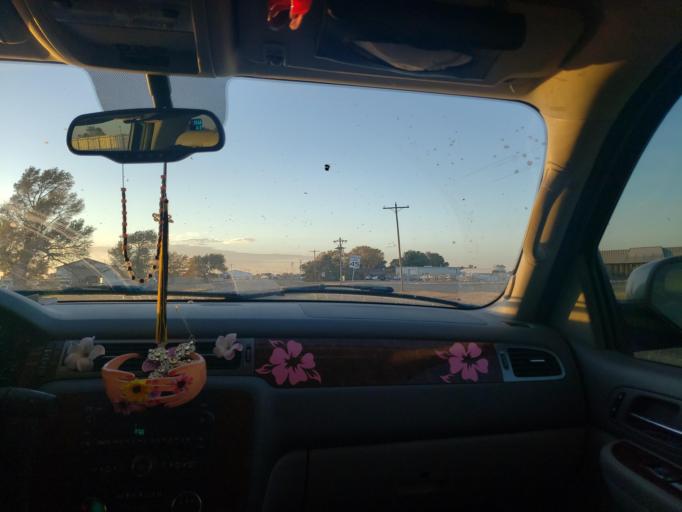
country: US
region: Kansas
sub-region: Finney County
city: Garden City
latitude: 37.9805
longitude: -100.8984
